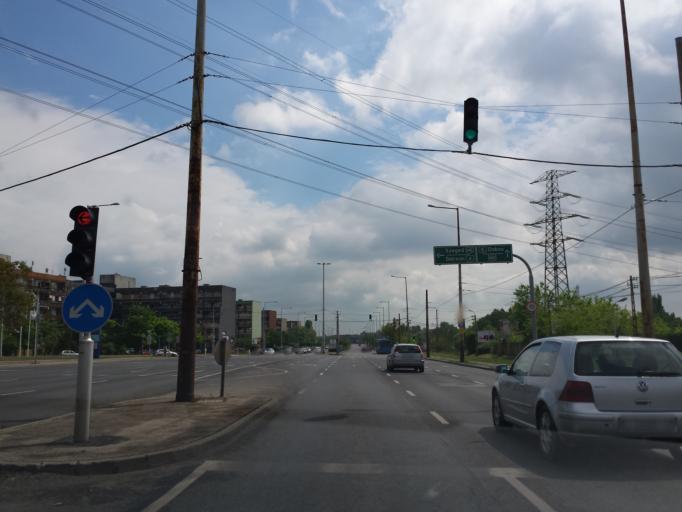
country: HU
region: Budapest
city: Budapest XX. keruelet
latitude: 47.4427
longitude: 19.0932
